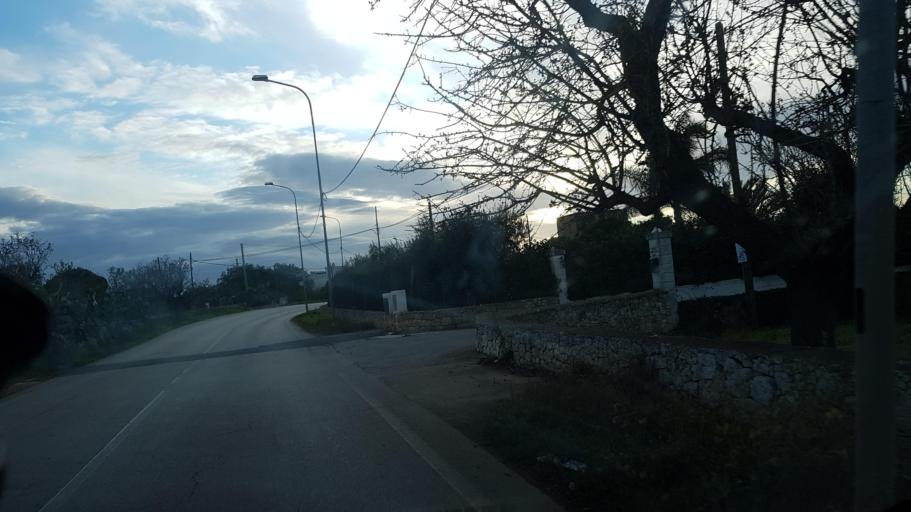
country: IT
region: Apulia
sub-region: Provincia di Brindisi
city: San Vito dei Normanni
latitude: 40.6502
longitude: 17.6991
